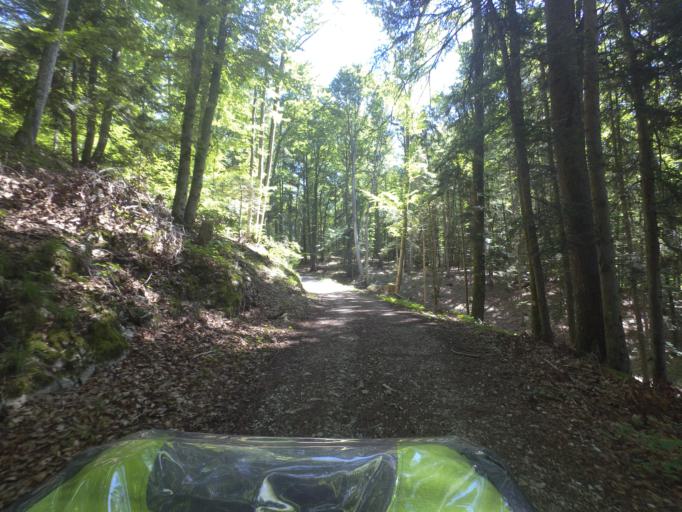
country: AT
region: Salzburg
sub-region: Politischer Bezirk Hallein
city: Oberalm
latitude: 47.7143
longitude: 13.1125
